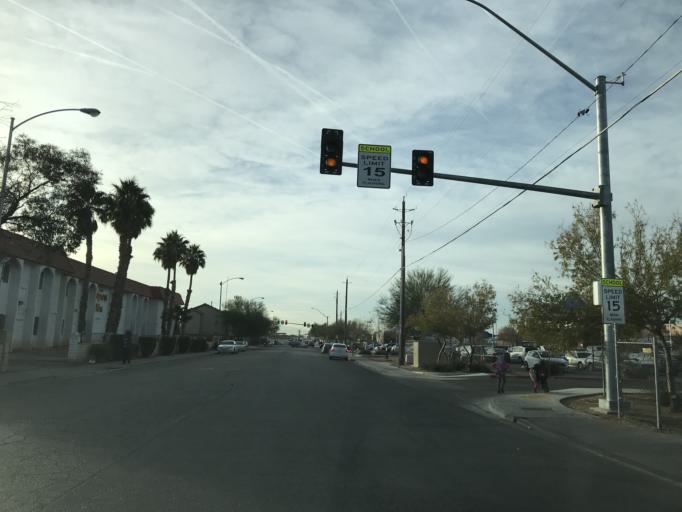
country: US
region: Nevada
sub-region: Clark County
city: Nellis Air Force Base
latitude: 36.2400
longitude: -115.0665
